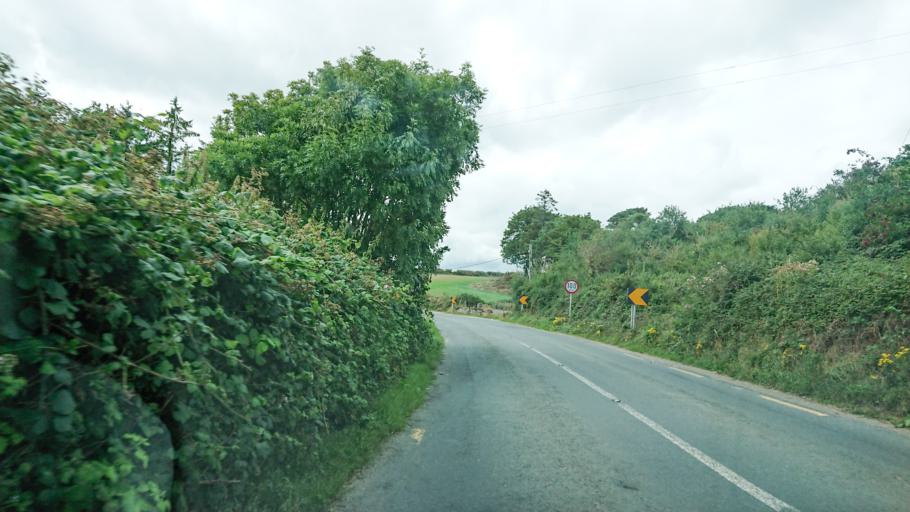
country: IE
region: Munster
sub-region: County Cork
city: Mallow
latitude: 52.1526
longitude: -8.5471
